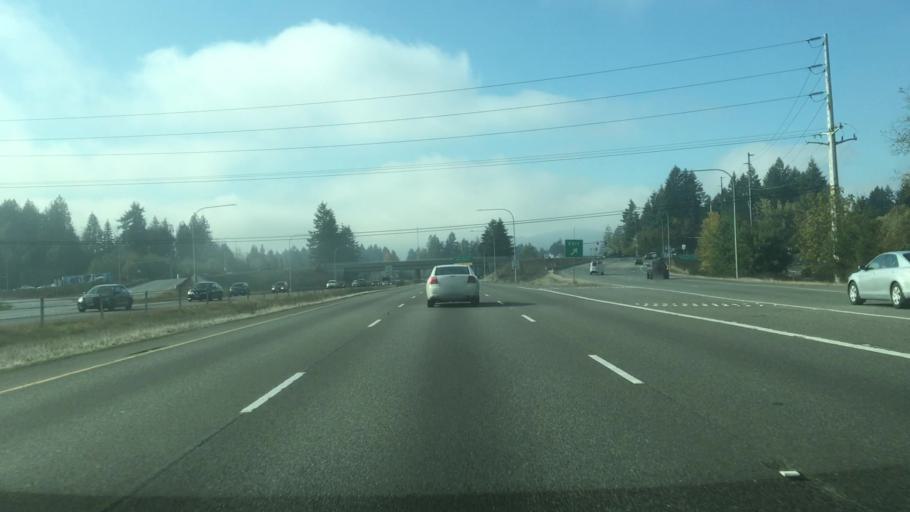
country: US
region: Washington
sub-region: Thurston County
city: Tumwater
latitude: 47.0259
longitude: -122.9193
